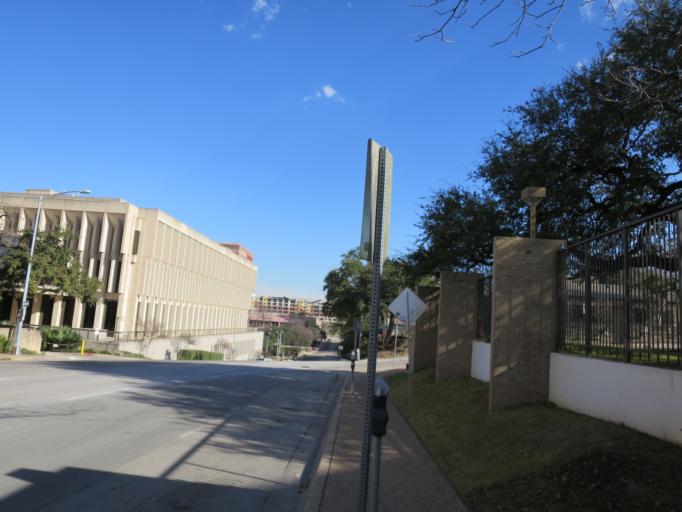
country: US
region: Texas
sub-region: Travis County
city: Austin
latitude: 30.2705
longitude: -97.7373
